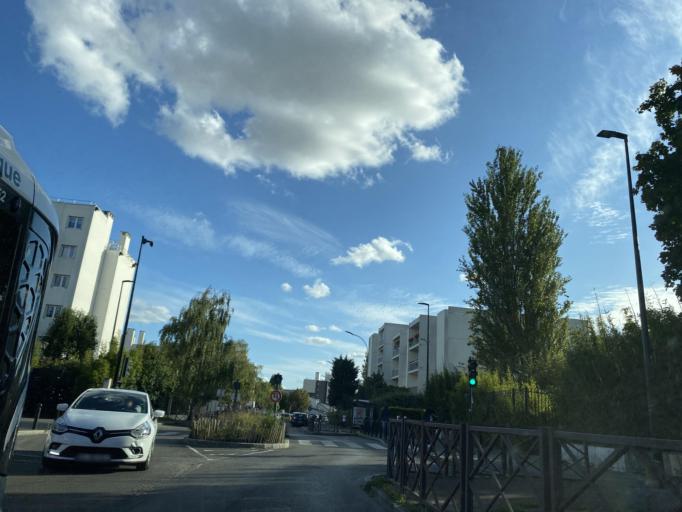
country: FR
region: Ile-de-France
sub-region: Departement des Yvelines
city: Sartrouville
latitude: 48.9448
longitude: 2.1946
